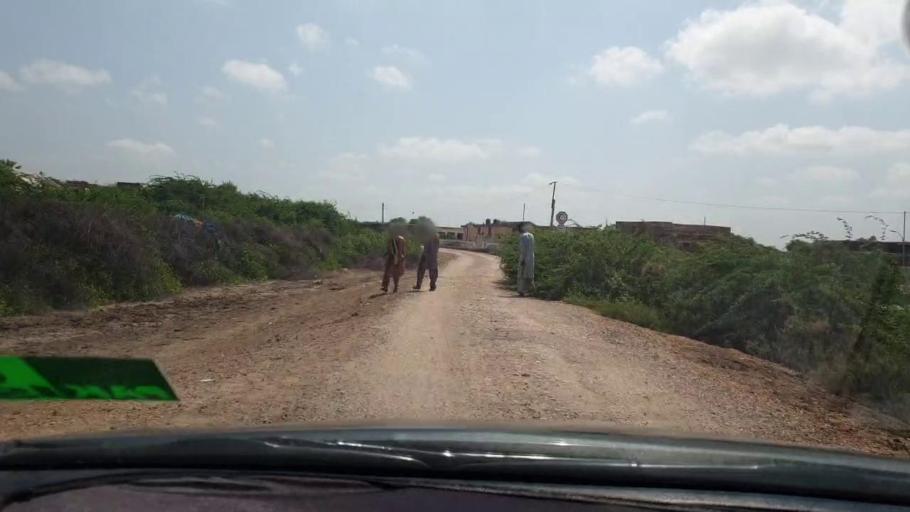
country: PK
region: Sindh
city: Digri
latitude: 24.9501
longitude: 69.1130
